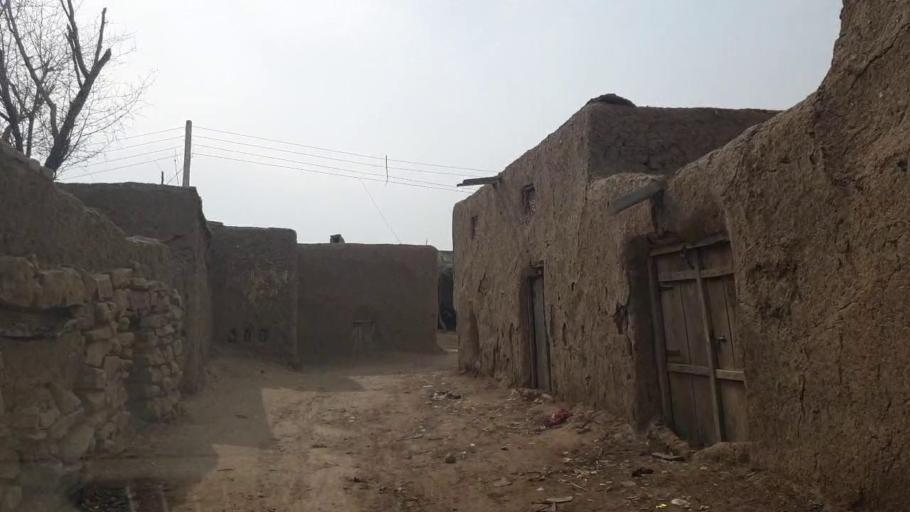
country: PK
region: Sindh
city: Sann
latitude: 25.9649
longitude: 68.1524
